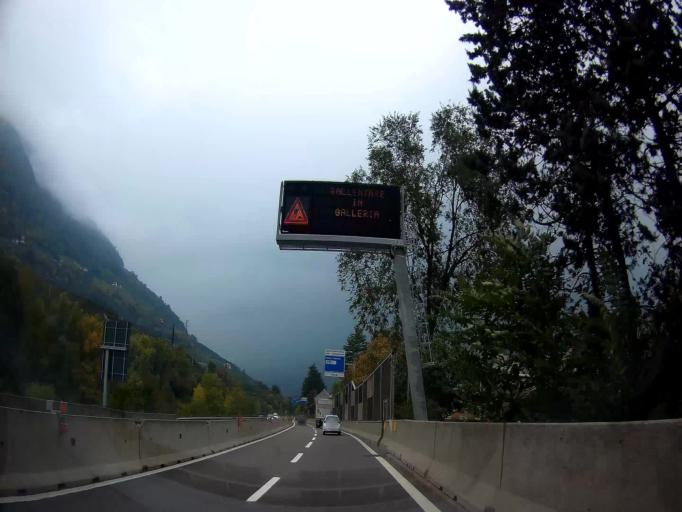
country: IT
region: Trentino-Alto Adige
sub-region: Bolzano
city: Marlengo
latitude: 46.6651
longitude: 11.1431
